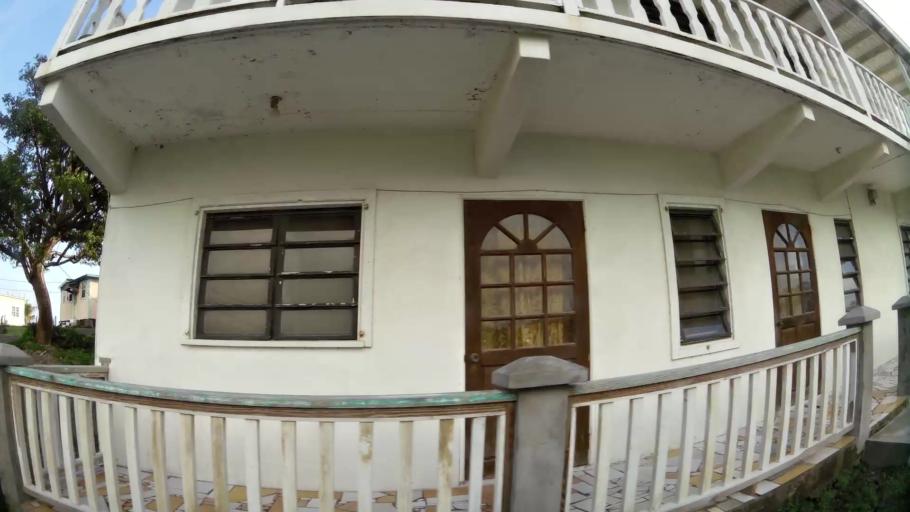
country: KN
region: Saint John Figtree
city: Fig Tree
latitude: 17.1167
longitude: -62.6048
